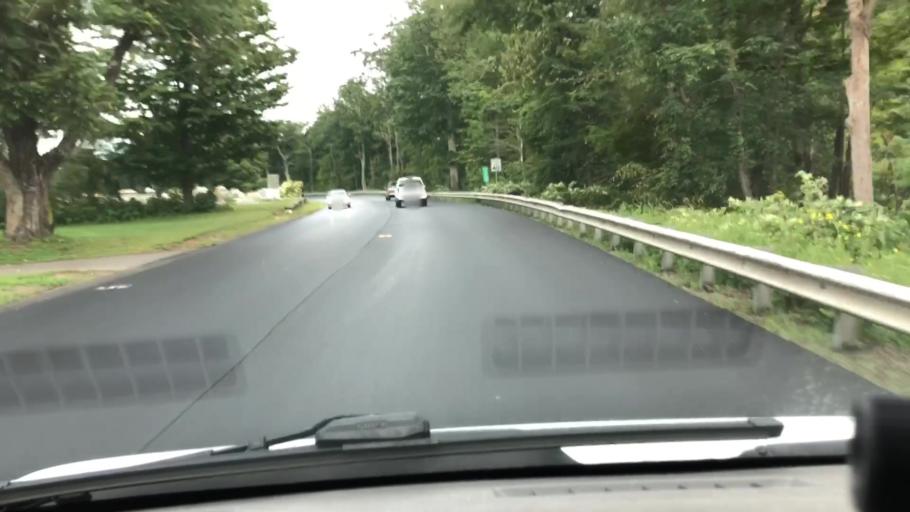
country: US
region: Massachusetts
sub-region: Franklin County
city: Charlemont
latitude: 42.6172
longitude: -72.8351
